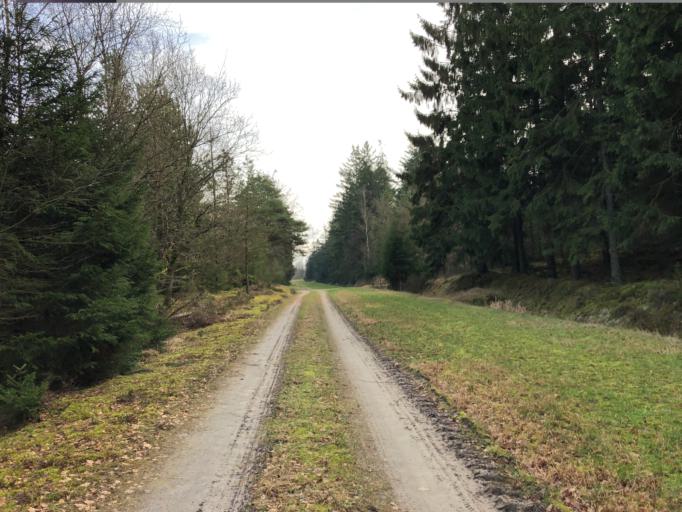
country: DK
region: Central Jutland
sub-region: Holstebro Kommune
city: Ulfborg
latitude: 56.2599
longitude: 8.3895
